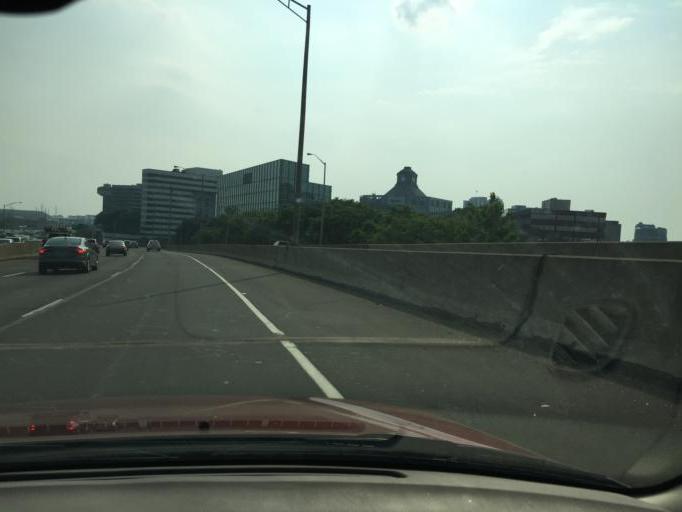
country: US
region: Connecticut
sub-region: Fairfield County
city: Stamford
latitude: 41.0542
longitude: -73.5273
